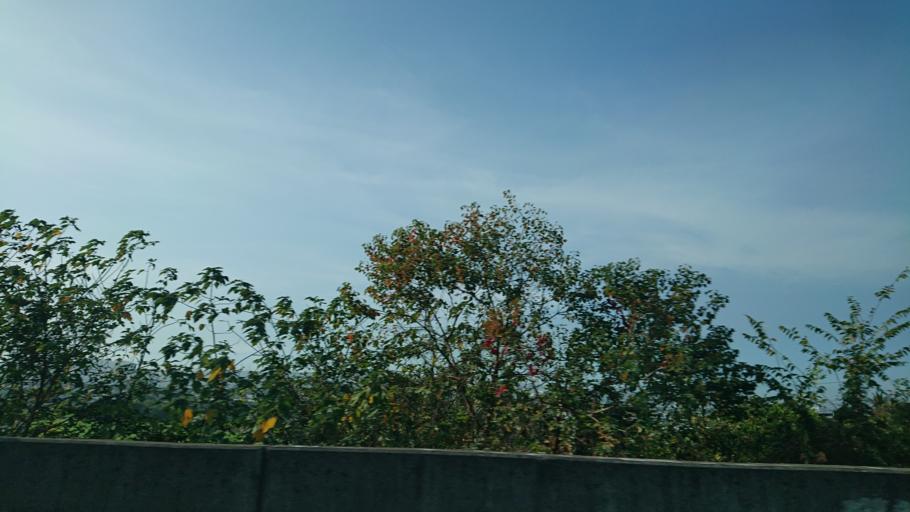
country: TW
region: Taiwan
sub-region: Taichung City
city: Taichung
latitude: 24.1909
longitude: 120.6386
